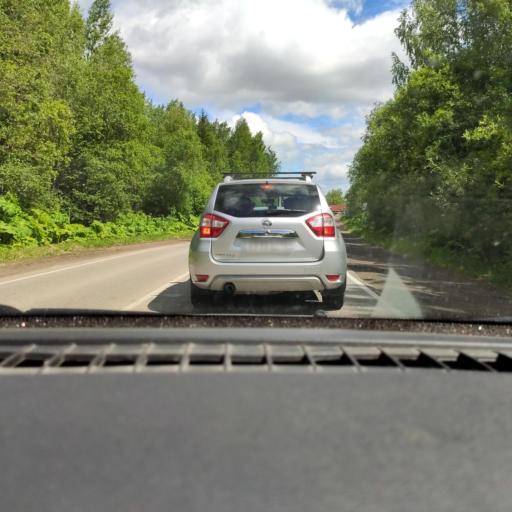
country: RU
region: Perm
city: Overyata
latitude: 58.1121
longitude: 55.8304
